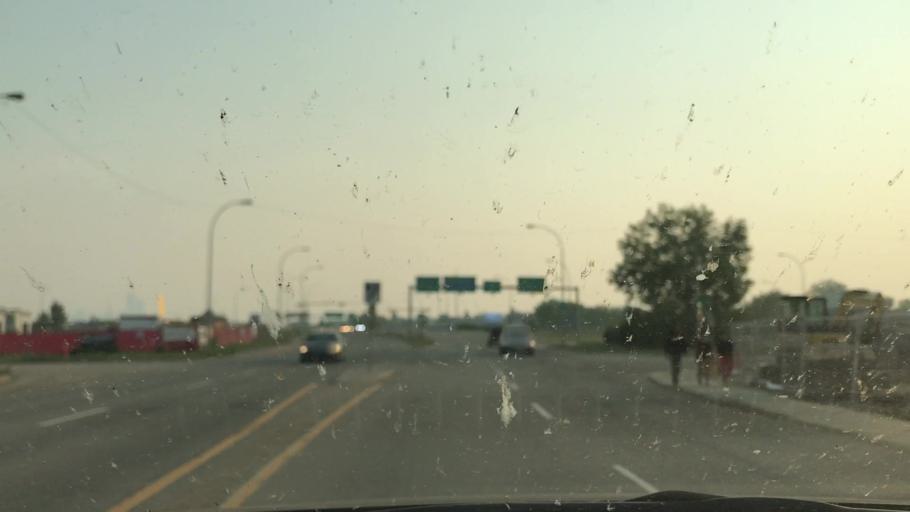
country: CA
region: Alberta
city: Edmonton
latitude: 53.5821
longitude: -113.4491
